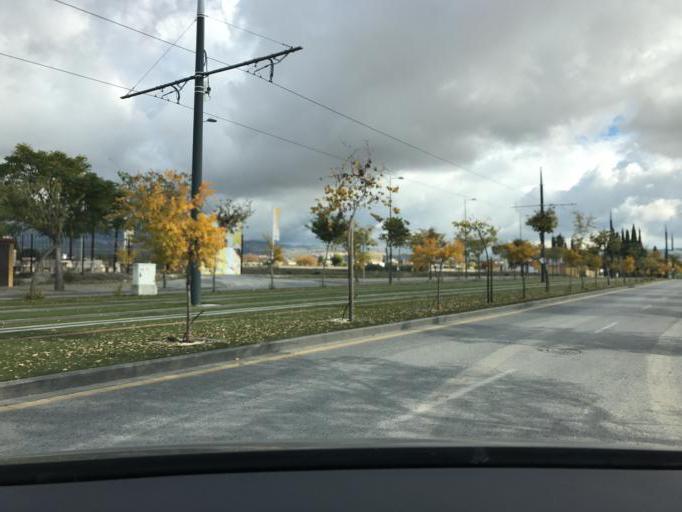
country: ES
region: Andalusia
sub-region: Provincia de Granada
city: Maracena
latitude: 37.2160
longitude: -3.6399
